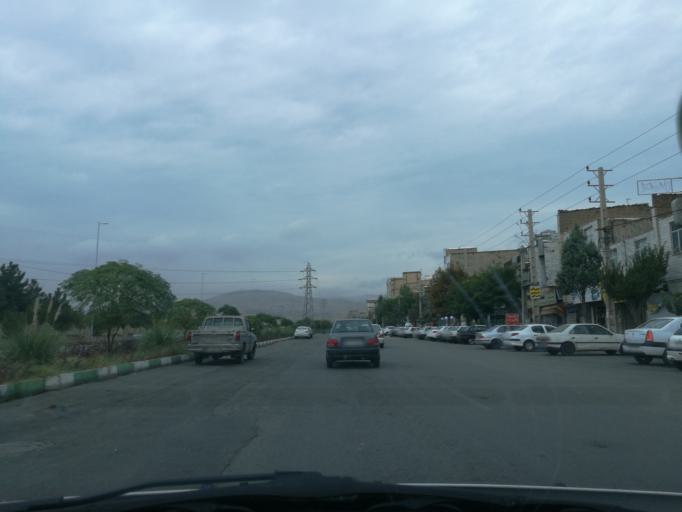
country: IR
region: Alborz
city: Karaj
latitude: 35.8483
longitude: 50.9161
